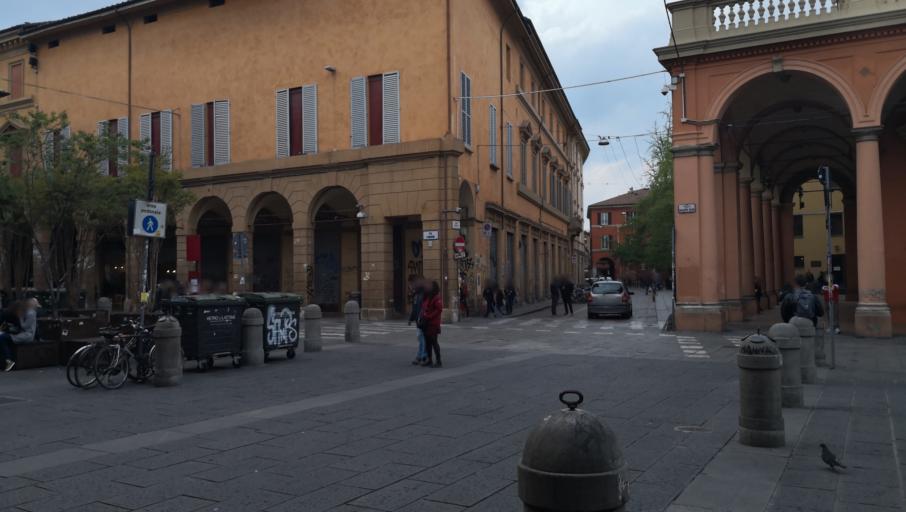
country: IT
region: Emilia-Romagna
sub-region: Provincia di Bologna
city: Bologna
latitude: 44.4962
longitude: 11.3506
